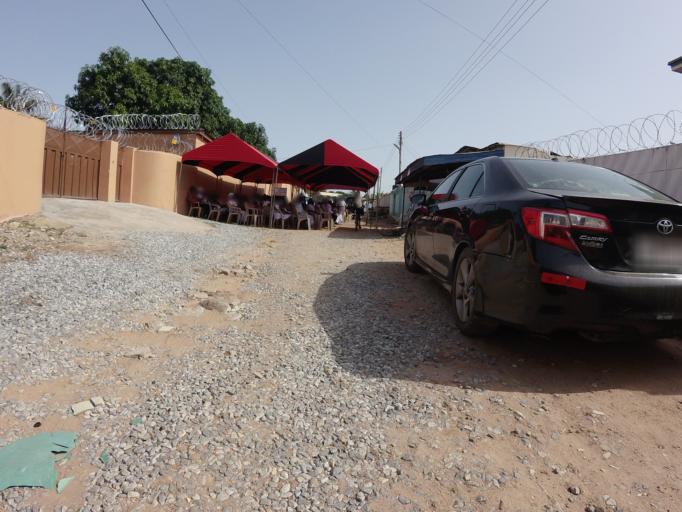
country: GH
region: Greater Accra
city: Dome
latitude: 5.6139
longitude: -0.2415
